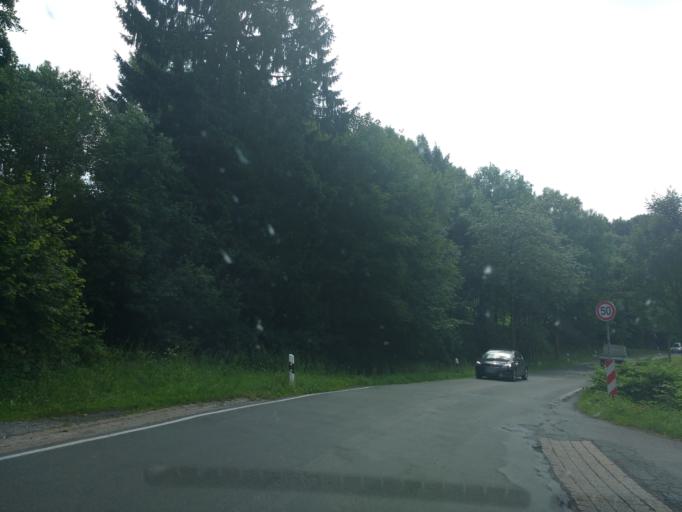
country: DE
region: North Rhine-Westphalia
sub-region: Regierungsbezirk Detmold
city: Dorentrup
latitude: 52.0554
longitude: 9.0560
